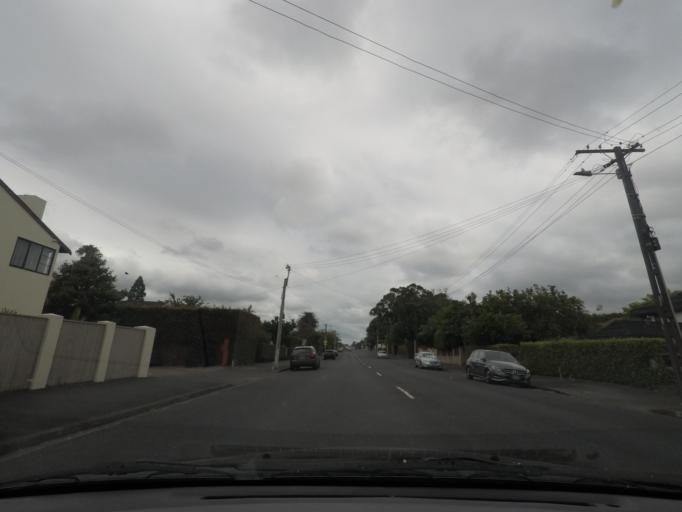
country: NZ
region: Auckland
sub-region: Auckland
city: Auckland
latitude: -36.8812
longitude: 174.7914
